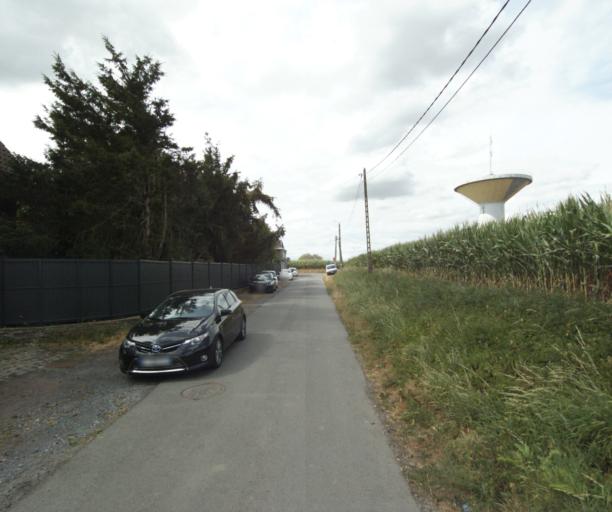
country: FR
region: Nord-Pas-de-Calais
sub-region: Departement du Nord
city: Bousbecque
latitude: 50.7664
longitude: 3.1025
